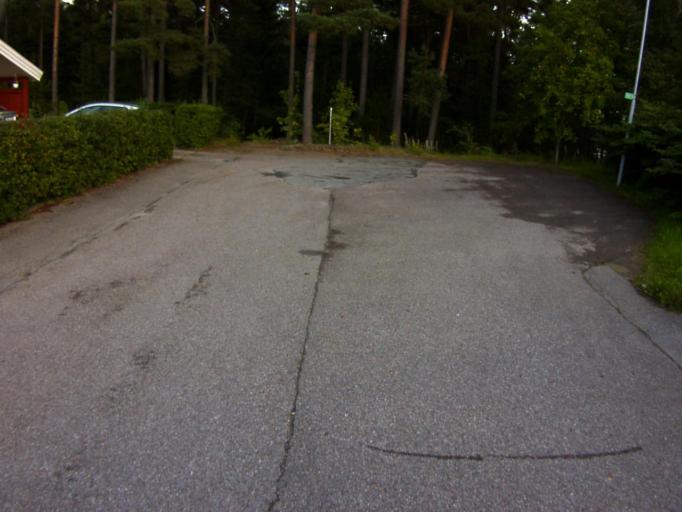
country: SE
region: Soedermanland
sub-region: Eskilstuna Kommun
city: Eskilstuna
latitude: 59.3852
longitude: 16.5467
